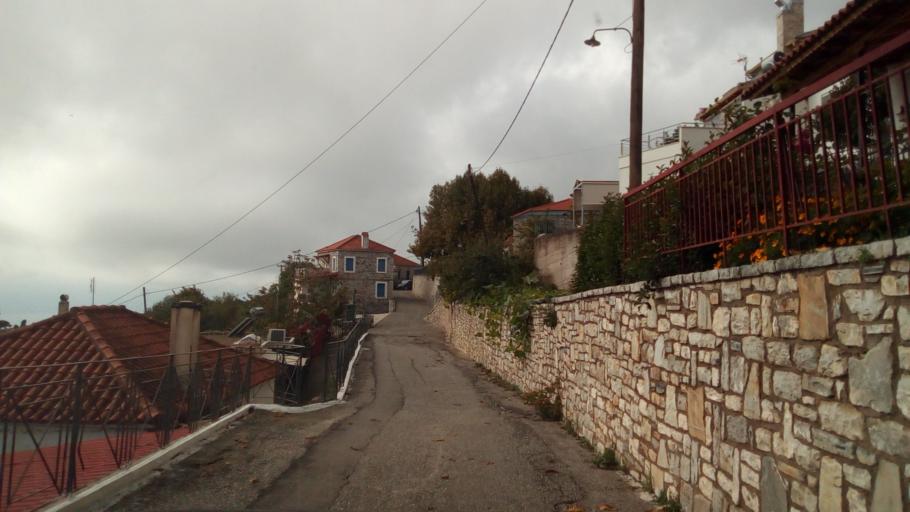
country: GR
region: West Greece
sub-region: Nomos Aitolias kai Akarnanias
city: Nafpaktos
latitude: 38.4500
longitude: 21.9683
